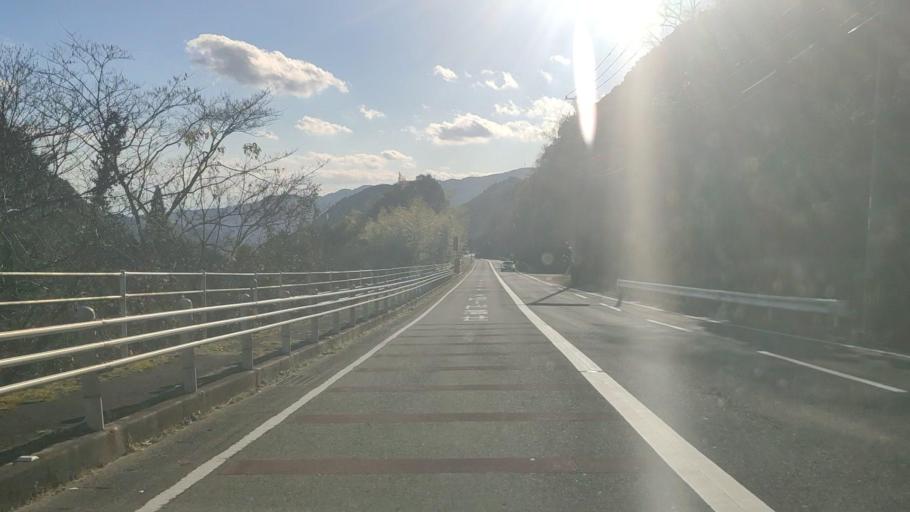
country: JP
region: Saga Prefecture
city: Kanzakimachi-kanzaki
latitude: 33.3844
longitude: 130.2604
